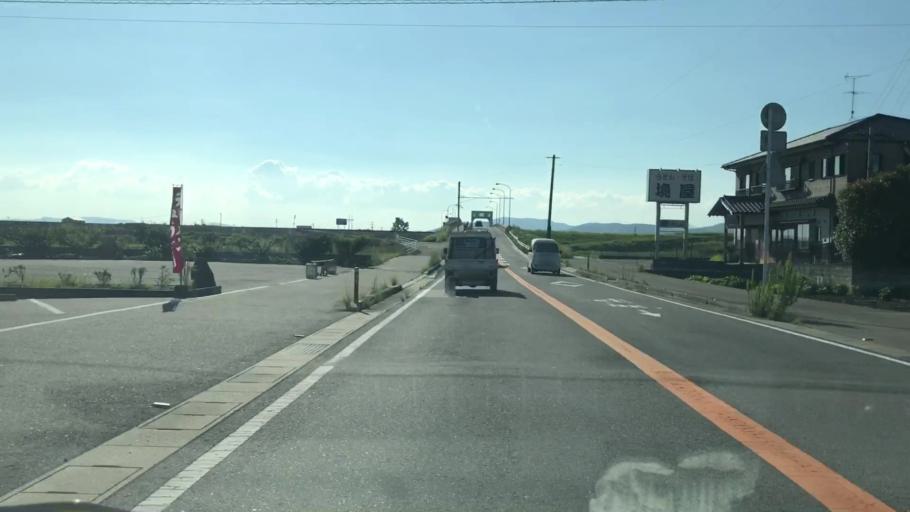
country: JP
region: Saga Prefecture
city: Saga-shi
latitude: 33.2194
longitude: 130.2552
